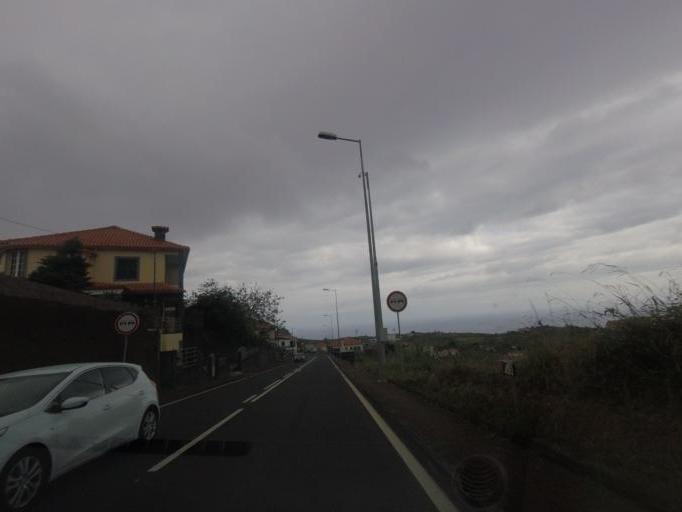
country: PT
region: Madeira
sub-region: Santana
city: Santana
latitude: 32.8198
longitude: -16.8877
